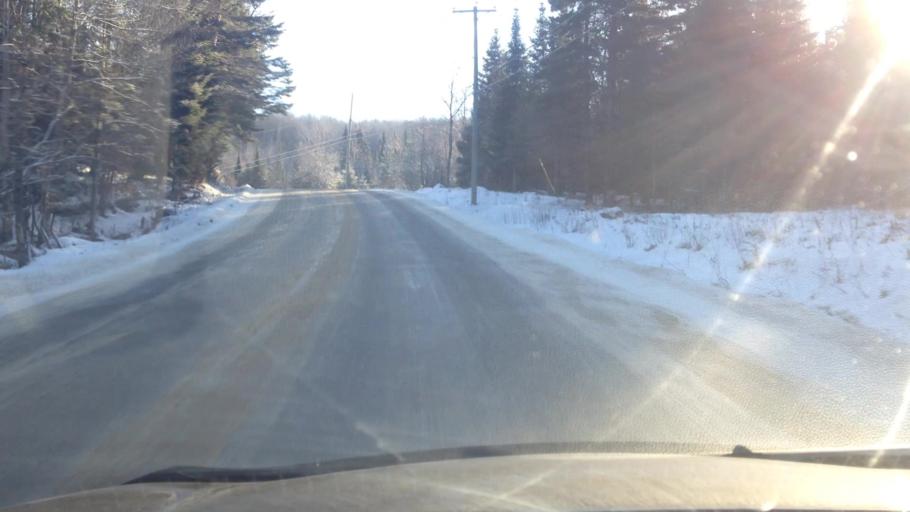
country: CA
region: Quebec
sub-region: Laurentides
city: Brownsburg-Chatham
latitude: 45.9206
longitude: -74.5250
